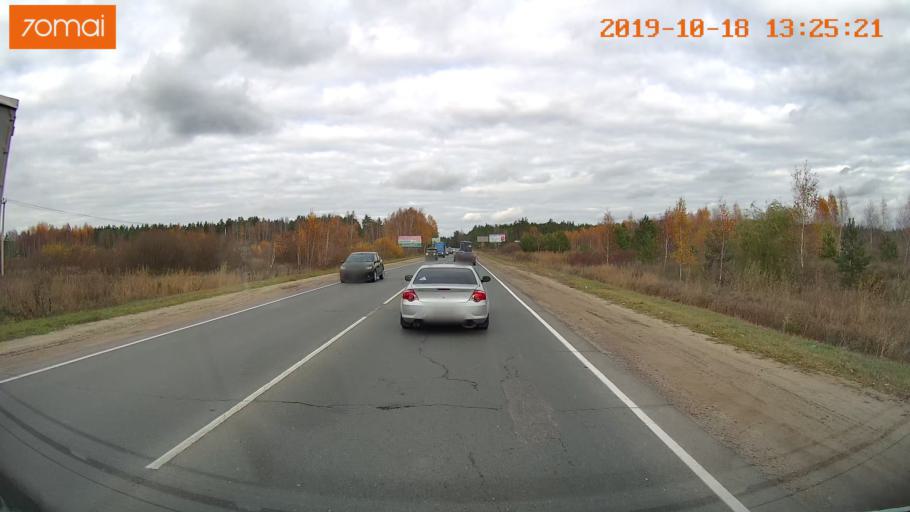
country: RU
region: Rjazan
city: Polyany
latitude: 54.7420
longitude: 39.8408
